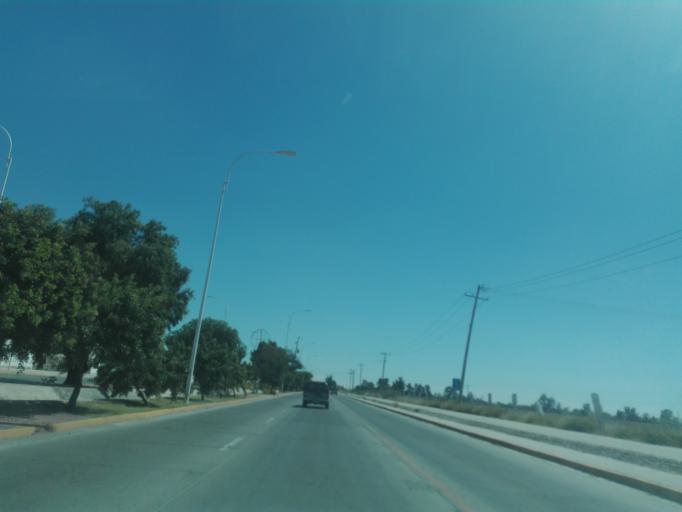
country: MX
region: Guanajuato
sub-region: Leon
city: San Jose de Duran (Los Troncoso)
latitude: 21.0786
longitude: -101.6560
